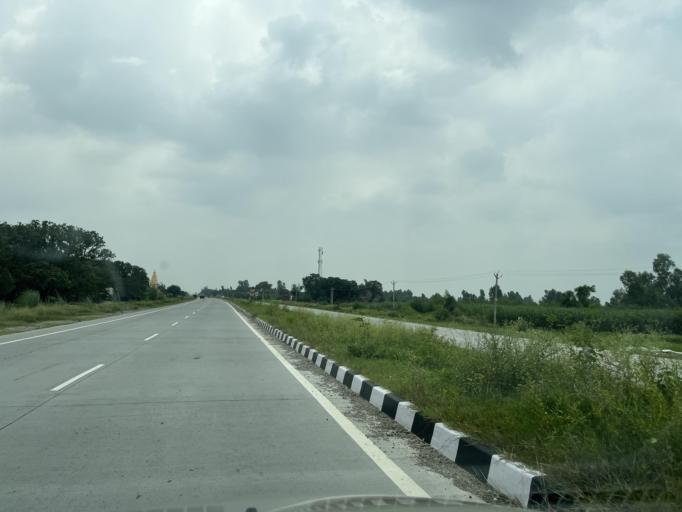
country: IN
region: Uttar Pradesh
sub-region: Bijnor
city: Najibabad
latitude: 29.5524
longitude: 78.3392
